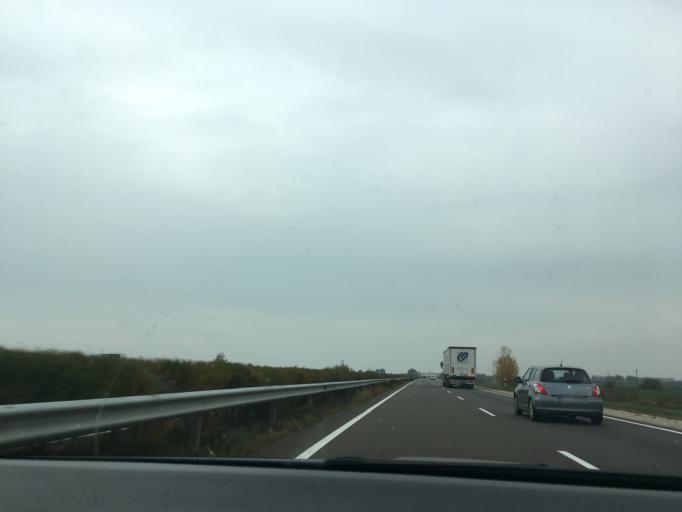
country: HU
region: Pest
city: Cegled
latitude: 47.1926
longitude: 19.8430
